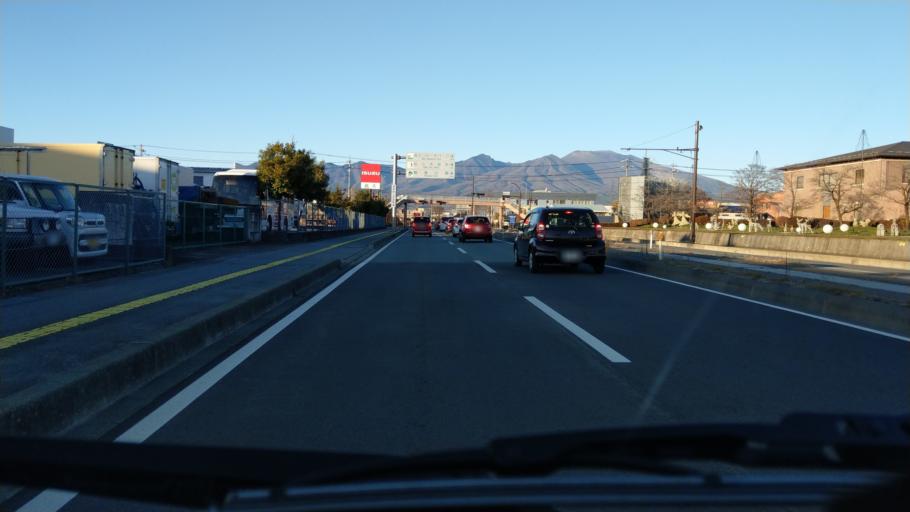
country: JP
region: Nagano
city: Saku
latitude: 36.2555
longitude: 138.4677
